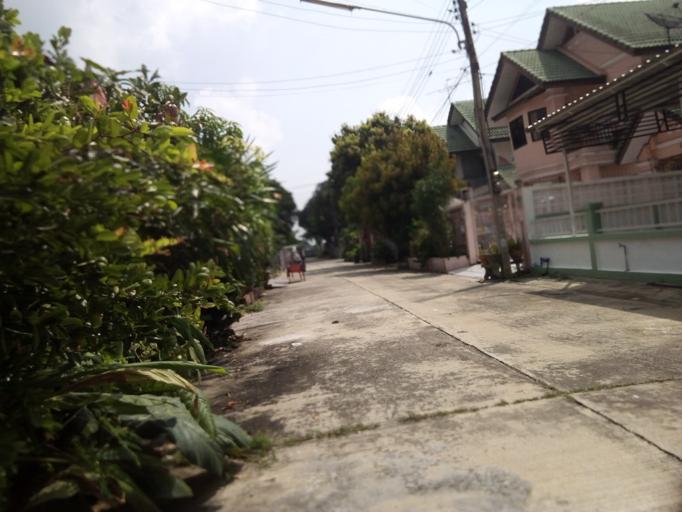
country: TH
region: Pathum Thani
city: Nong Suea
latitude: 14.0569
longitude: 100.8515
